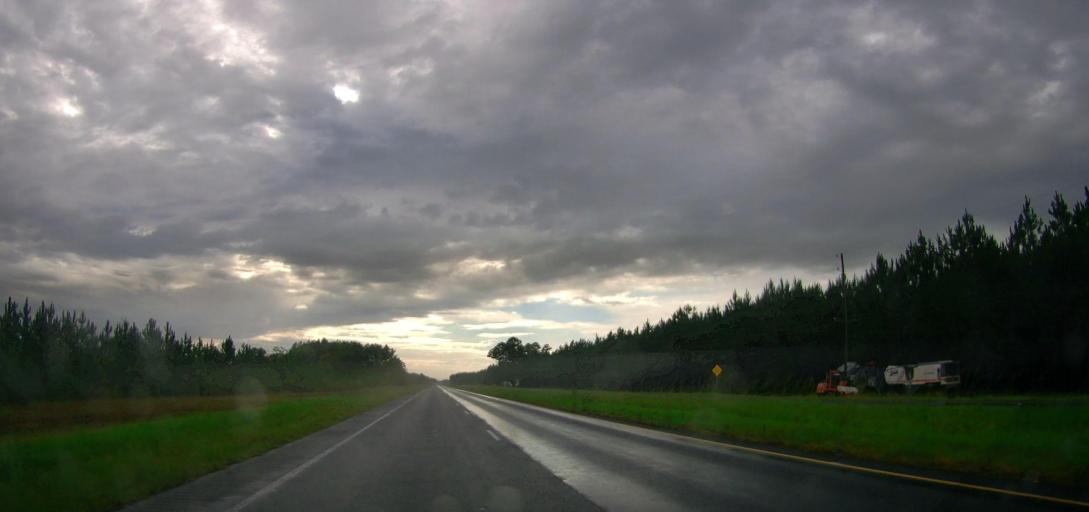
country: US
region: Georgia
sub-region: Ware County
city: Deenwood
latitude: 31.2566
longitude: -82.4921
